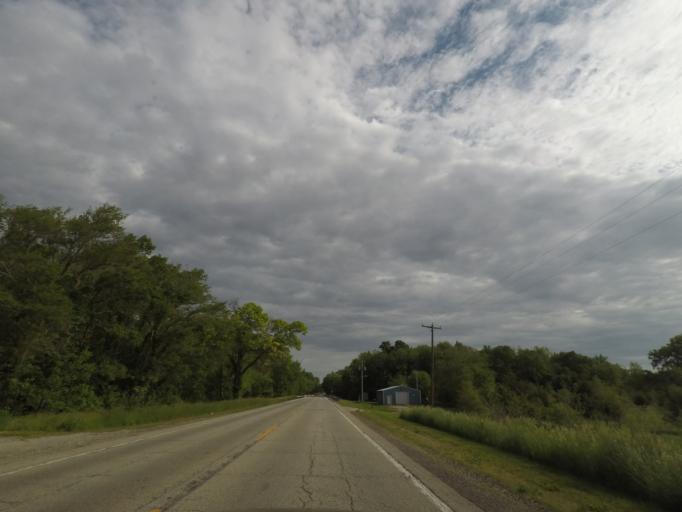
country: US
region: Illinois
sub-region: Logan County
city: Mount Pulaski
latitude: 40.0513
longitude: -89.2820
